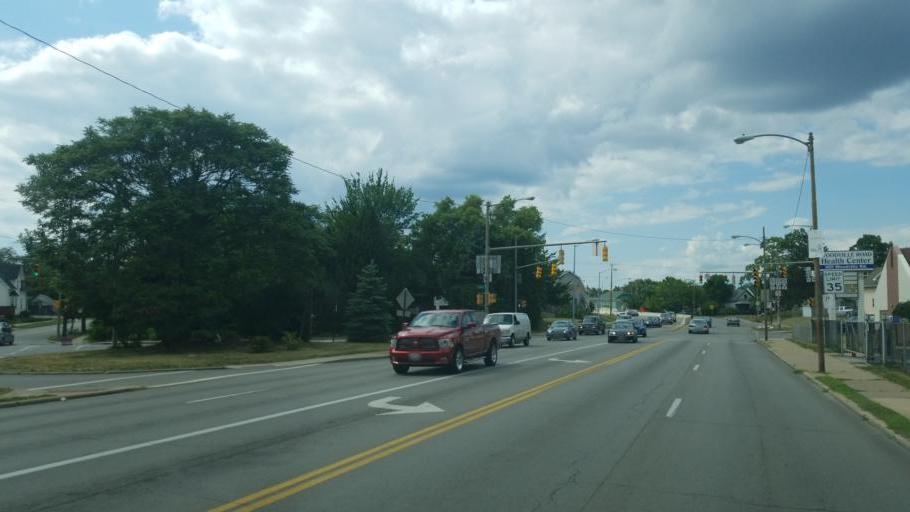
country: US
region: Ohio
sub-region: Lucas County
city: Oregon
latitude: 41.6399
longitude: -83.5247
